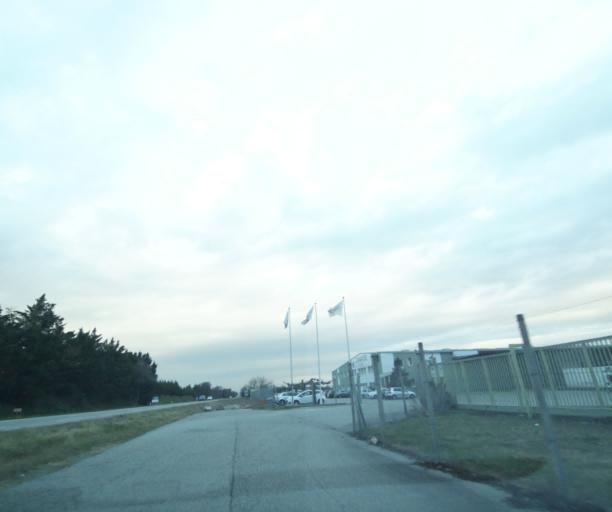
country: FR
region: Rhone-Alpes
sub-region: Departement de la Drome
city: Bourg-les-Valence
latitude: 44.9767
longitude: 4.8974
